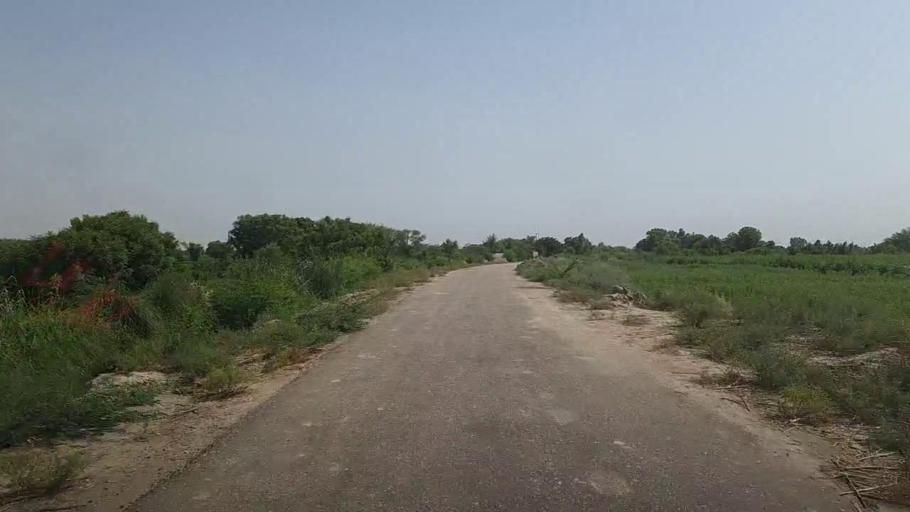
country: PK
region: Sindh
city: Pad Idan
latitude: 26.8019
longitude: 68.3325
